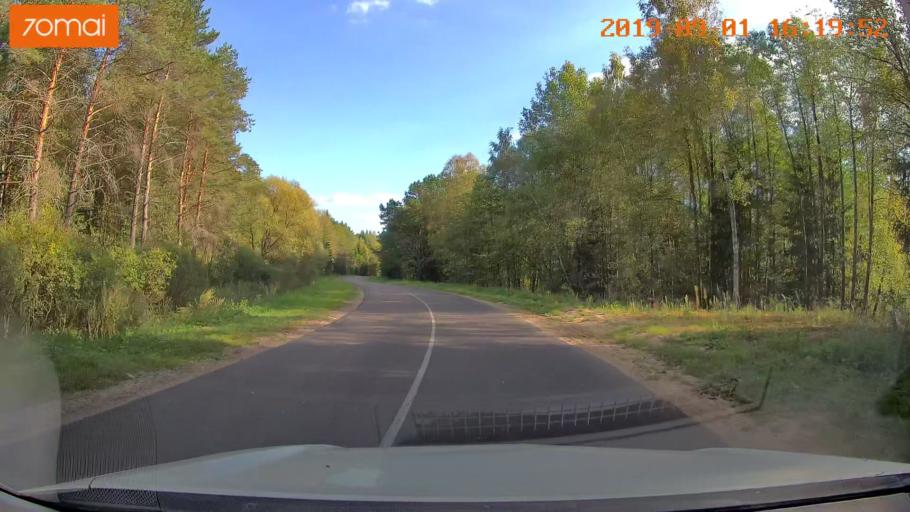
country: RU
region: Kaluga
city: Maloyaroslavets
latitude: 54.8849
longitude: 36.5295
